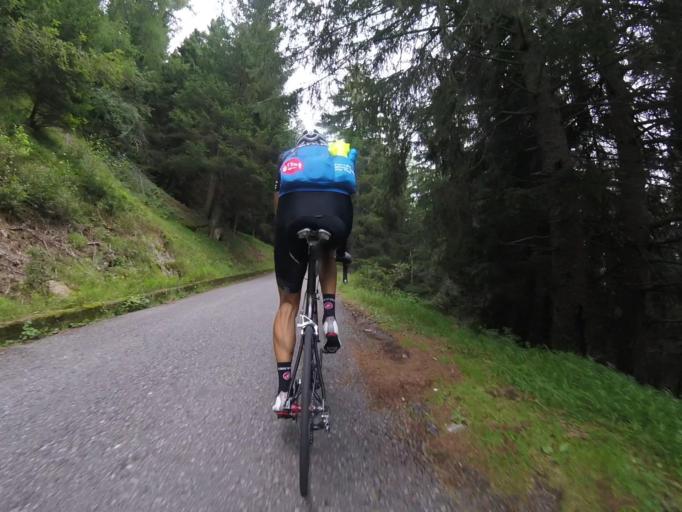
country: IT
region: Lombardy
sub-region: Provincia di Sondrio
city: Mazzo di Valtellina
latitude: 46.2521
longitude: 10.2888
